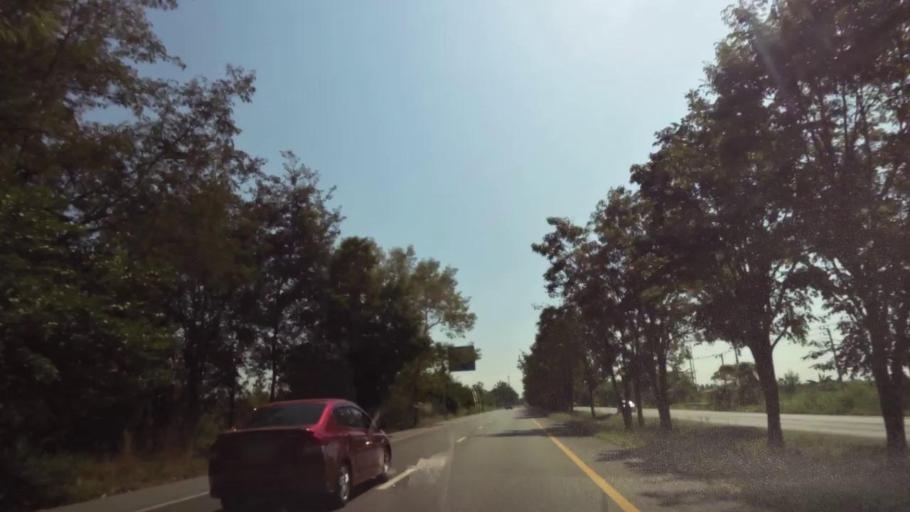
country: TH
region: Nakhon Sawan
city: Kao Liao
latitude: 15.8810
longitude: 100.1156
